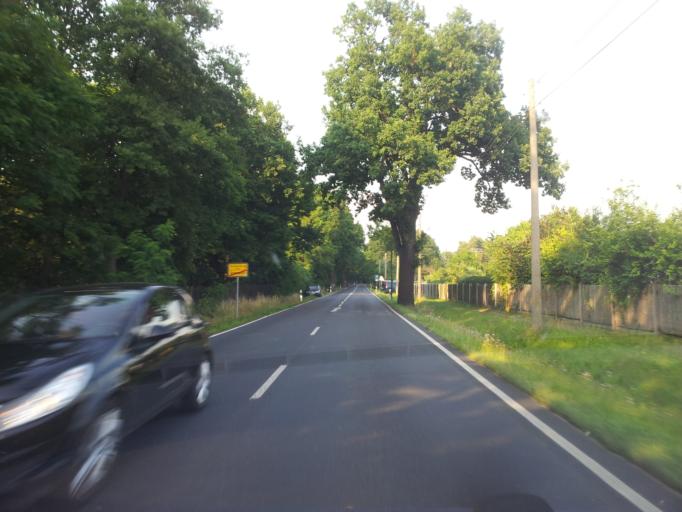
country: DE
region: Saxony
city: Schwepnitz
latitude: 51.3317
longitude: 13.9637
